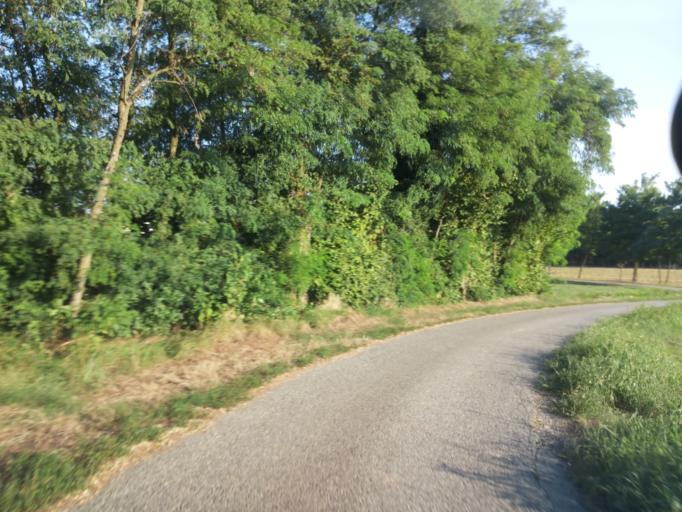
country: IT
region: Piedmont
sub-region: Provincia di Biella
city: Cavaglia
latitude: 45.3992
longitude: 8.1030
